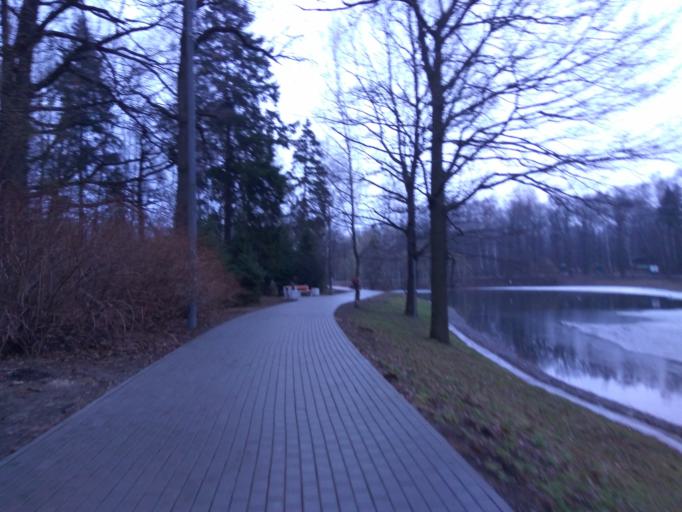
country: RU
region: Moscow
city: Vagonoremont
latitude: 55.9009
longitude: 37.5629
